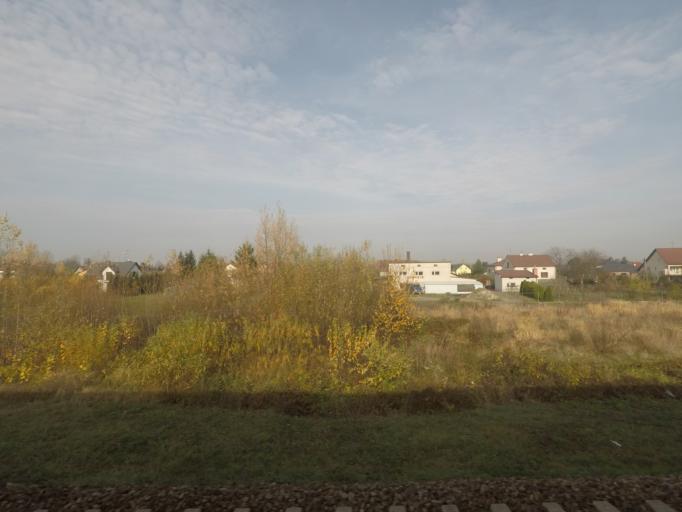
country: PL
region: Subcarpathian Voivodeship
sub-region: Powiat lancucki
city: Gluchow
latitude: 50.0835
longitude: 22.2770
